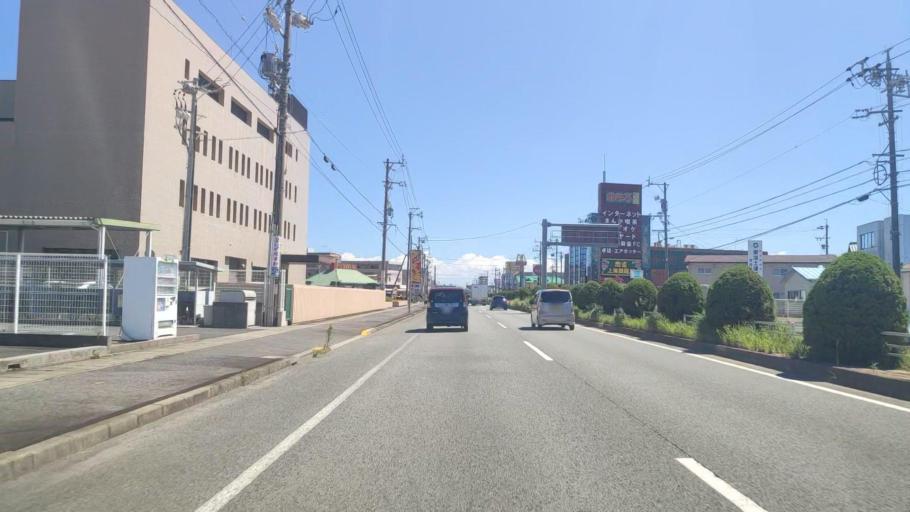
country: JP
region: Mie
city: Tsu-shi
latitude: 34.7511
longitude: 136.5217
